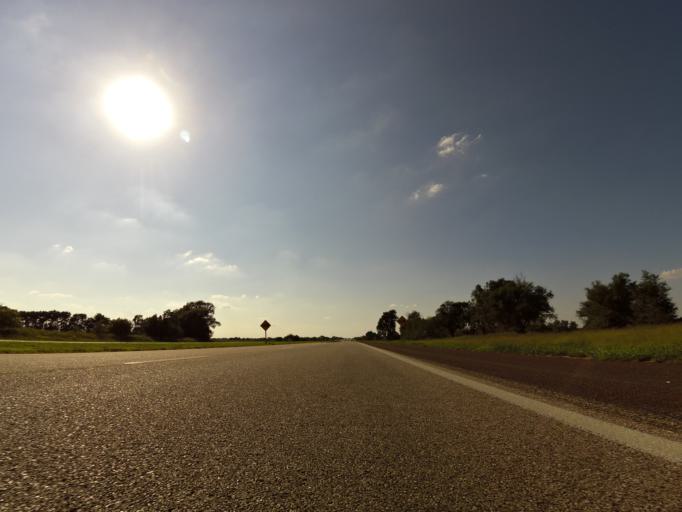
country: US
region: Kansas
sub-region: Reno County
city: Haven
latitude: 37.9190
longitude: -97.8271
